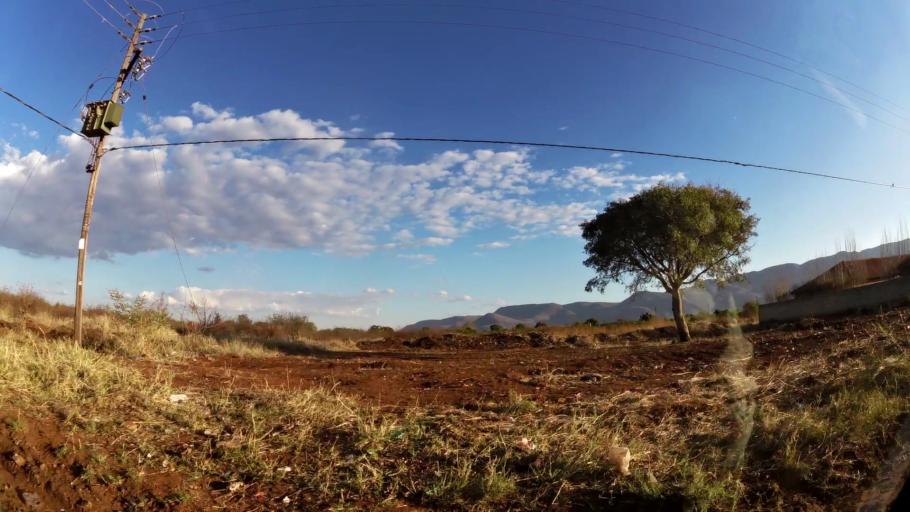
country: ZA
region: Limpopo
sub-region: Waterberg District Municipality
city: Mokopane
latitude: -24.1559
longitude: 28.9922
